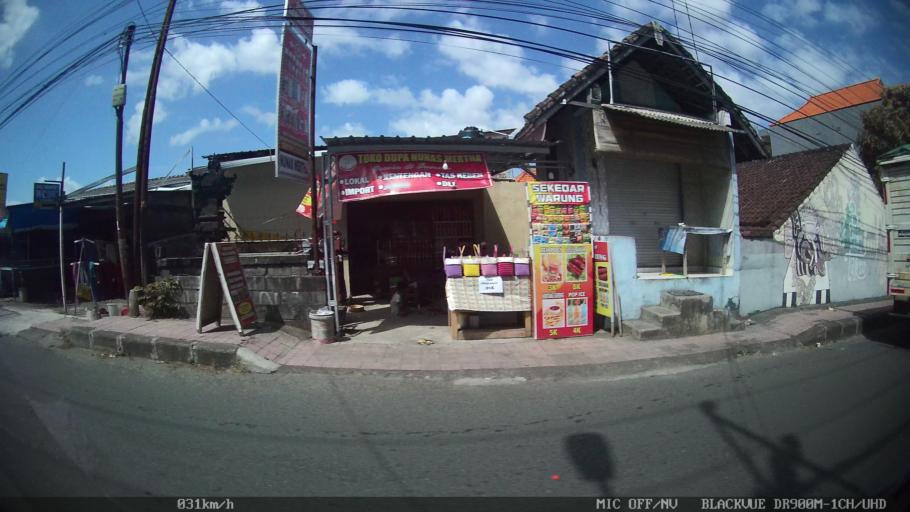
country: ID
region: Bali
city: Banjar Kertasari
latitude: -8.6414
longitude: 115.1855
